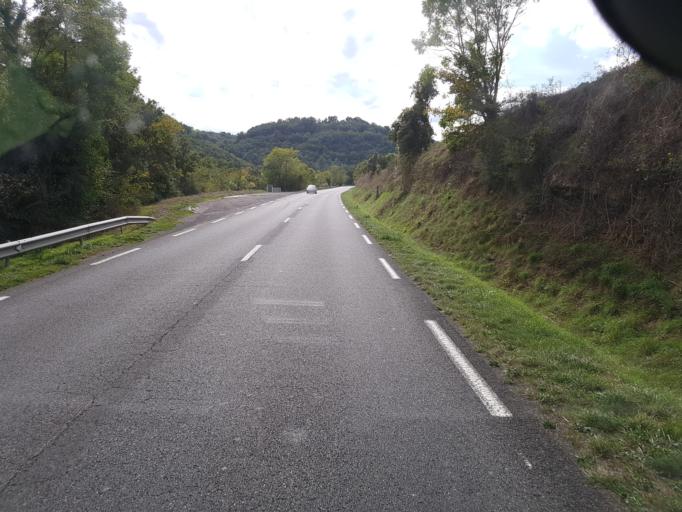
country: FR
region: Midi-Pyrenees
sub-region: Departement de l'Aveyron
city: Saint-Georges-de-Luzencon
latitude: 44.0491
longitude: 2.9776
